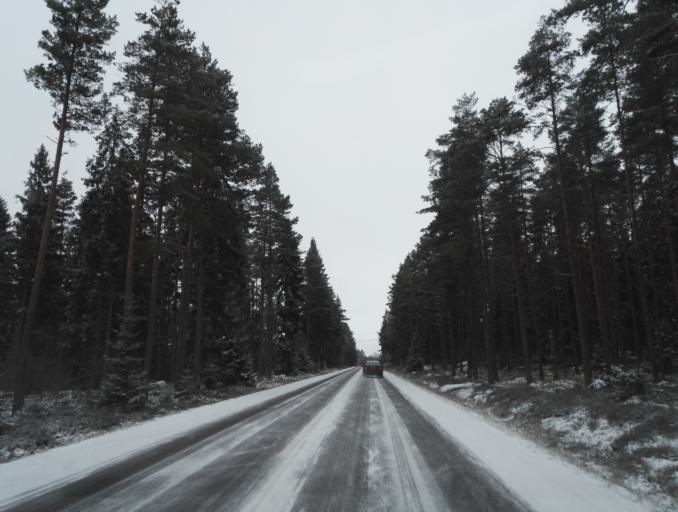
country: SE
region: Kronoberg
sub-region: Lessebo Kommun
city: Lessebo
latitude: 56.7940
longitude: 15.3159
